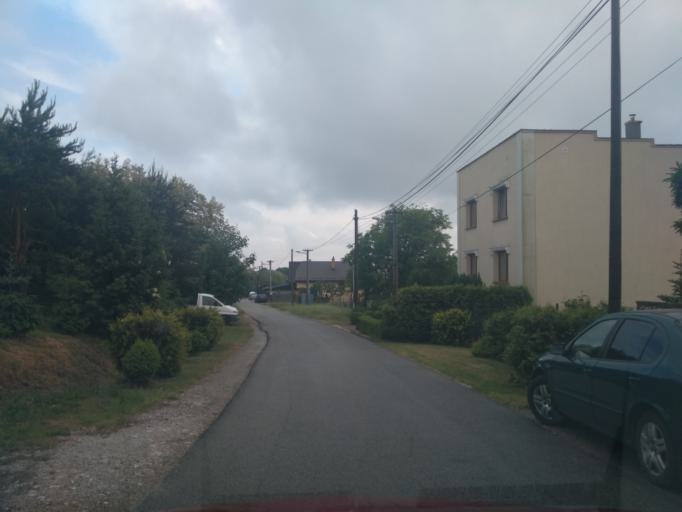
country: SK
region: Kosicky
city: Moldava nad Bodvou
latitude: 48.6901
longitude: 21.0743
